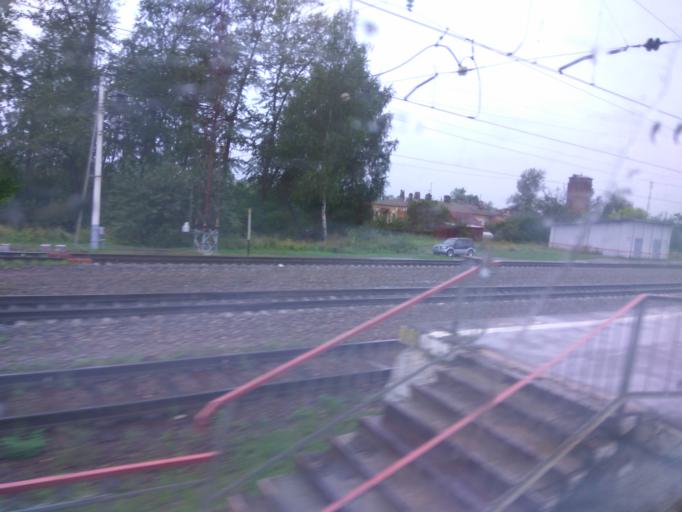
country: RU
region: Moskovskaya
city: Zhilevo
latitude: 54.9847
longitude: 38.0320
